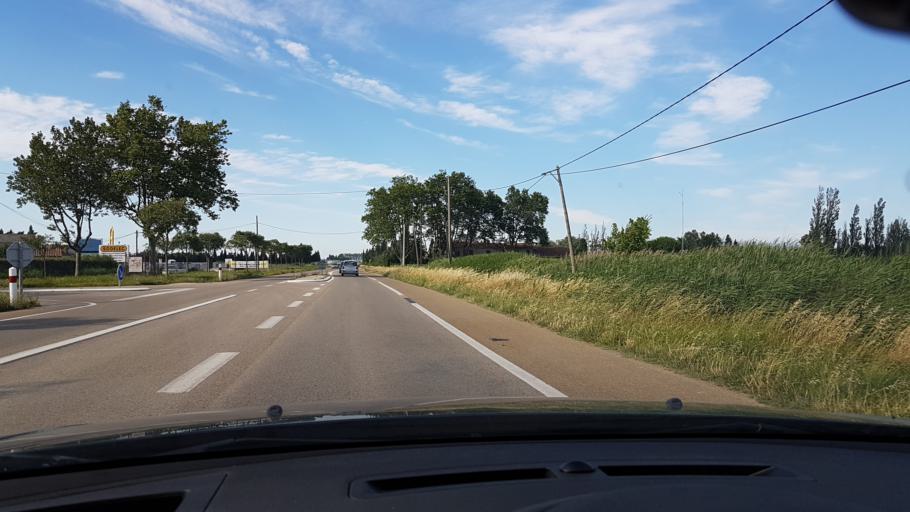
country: FR
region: Provence-Alpes-Cote d'Azur
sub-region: Departement des Bouches-du-Rhone
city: Graveson
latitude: 43.8766
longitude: 4.7741
